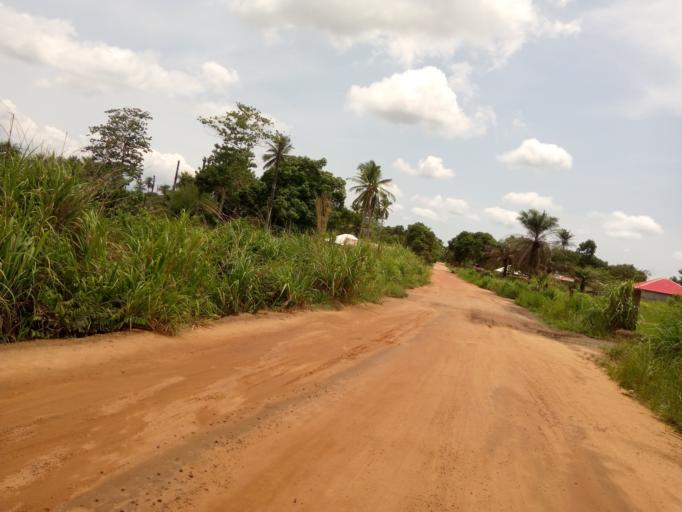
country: SL
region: Western Area
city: Waterloo
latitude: 8.3530
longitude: -12.9589
